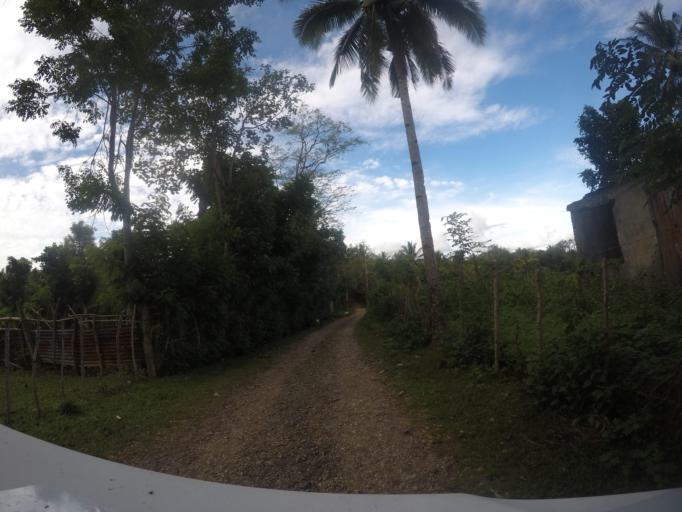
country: TL
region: Lautem
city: Lospalos
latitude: -8.5061
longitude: 126.9902
